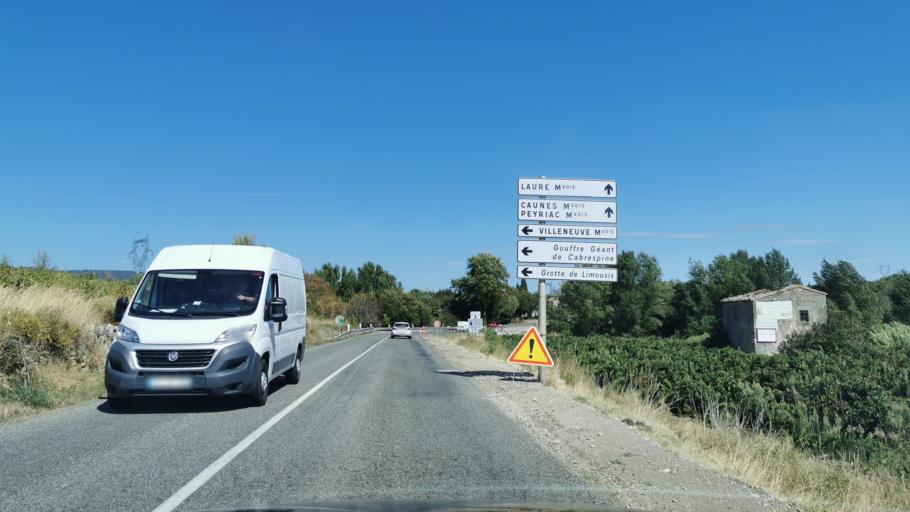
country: FR
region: Languedoc-Roussillon
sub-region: Departement de l'Aude
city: Conques-sur-Orbiel
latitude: 43.2993
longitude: 2.4617
